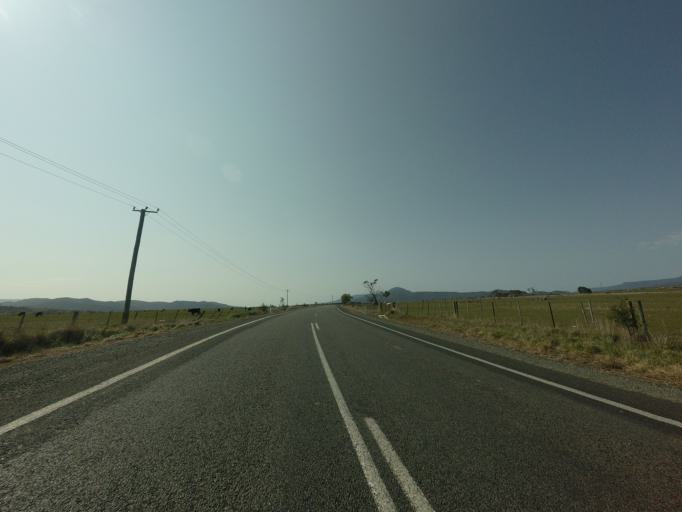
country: AU
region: Tasmania
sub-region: Northern Midlands
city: Evandale
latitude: -41.8035
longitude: 147.6845
